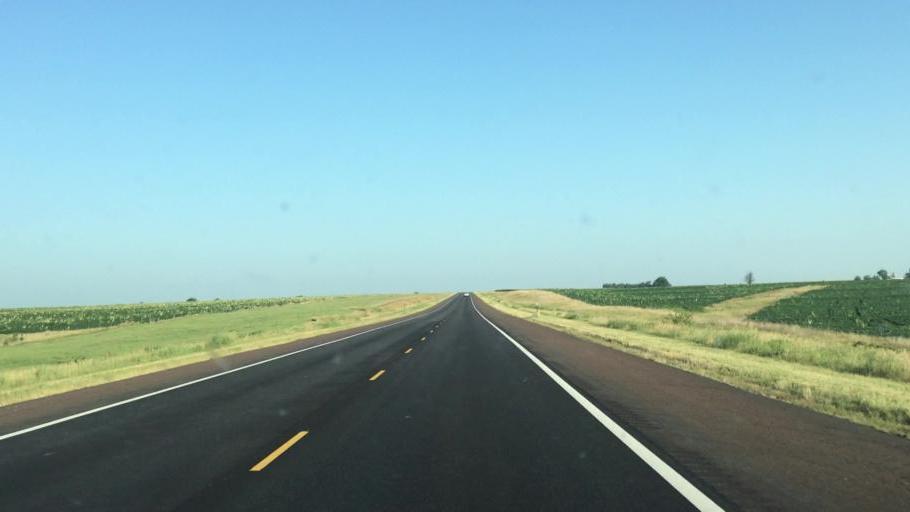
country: US
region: Kansas
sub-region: Nemaha County
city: Sabetha
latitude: 39.8583
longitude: -95.7590
